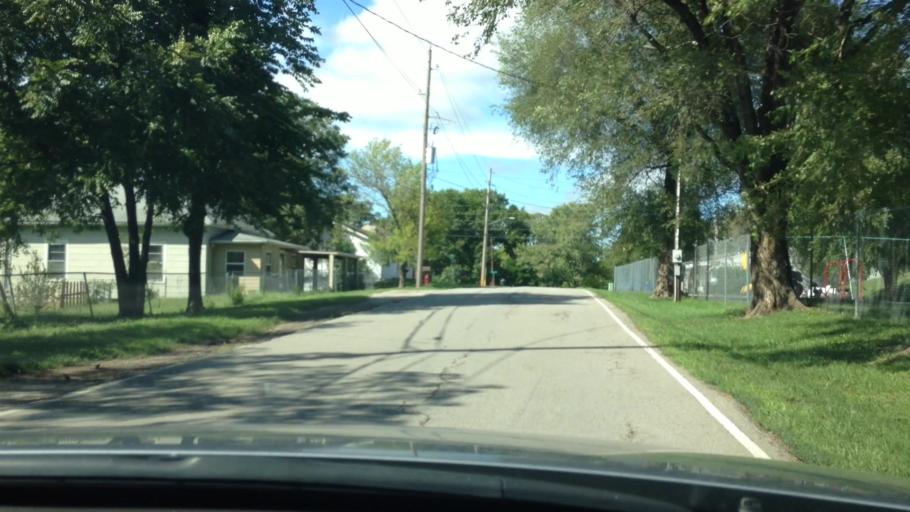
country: US
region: Missouri
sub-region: Platte County
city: Weatherby Lake
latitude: 39.3114
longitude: -94.6666
